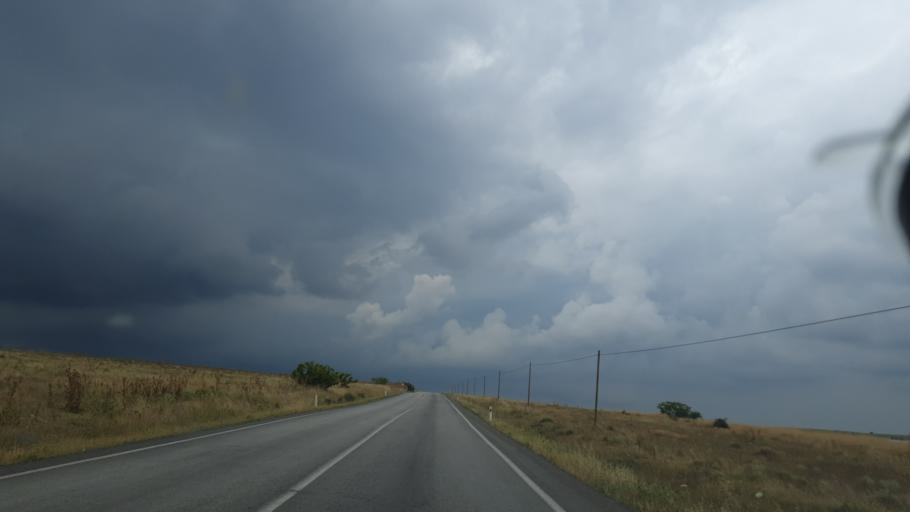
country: TR
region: Tekirdag
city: Hayrabolu
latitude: 41.2186
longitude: 27.0578
